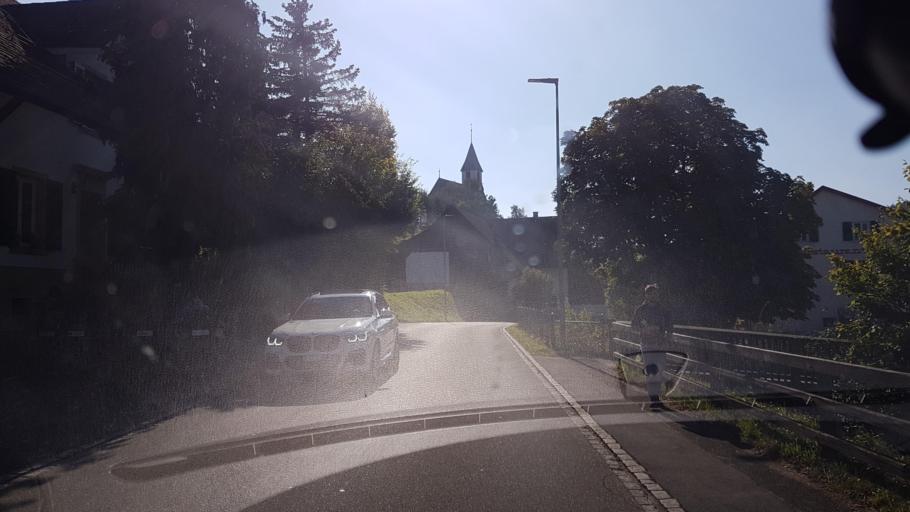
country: CH
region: Aargau
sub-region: Bezirk Laufenburg
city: Sulz
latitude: 47.4968
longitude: 8.0865
